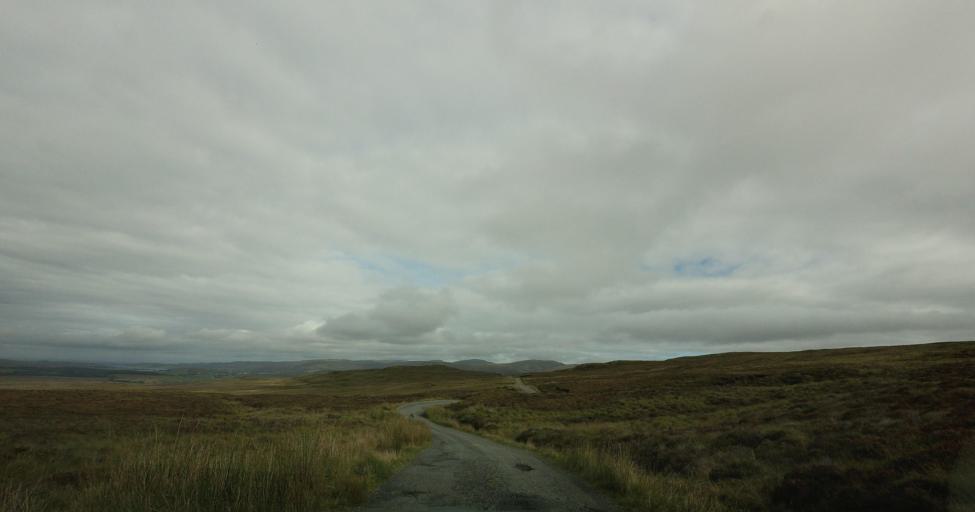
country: GB
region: Scotland
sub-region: Highland
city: Isle of Skye
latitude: 57.4023
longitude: -6.2689
